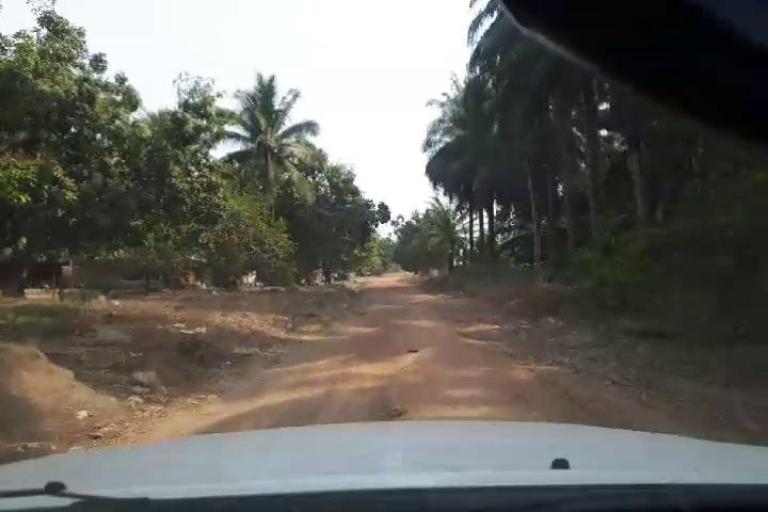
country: SL
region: Northern Province
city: Masingbi
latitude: 8.7863
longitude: -11.8714
